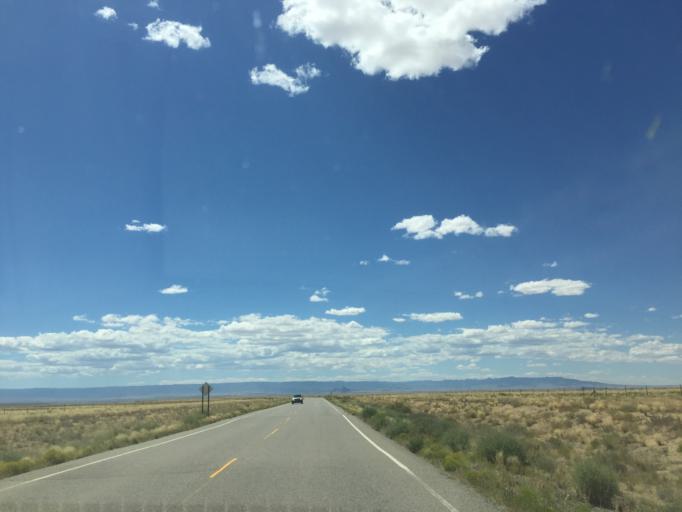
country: US
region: New Mexico
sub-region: San Juan County
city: Upper Fruitland
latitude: 36.4196
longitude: -108.4327
